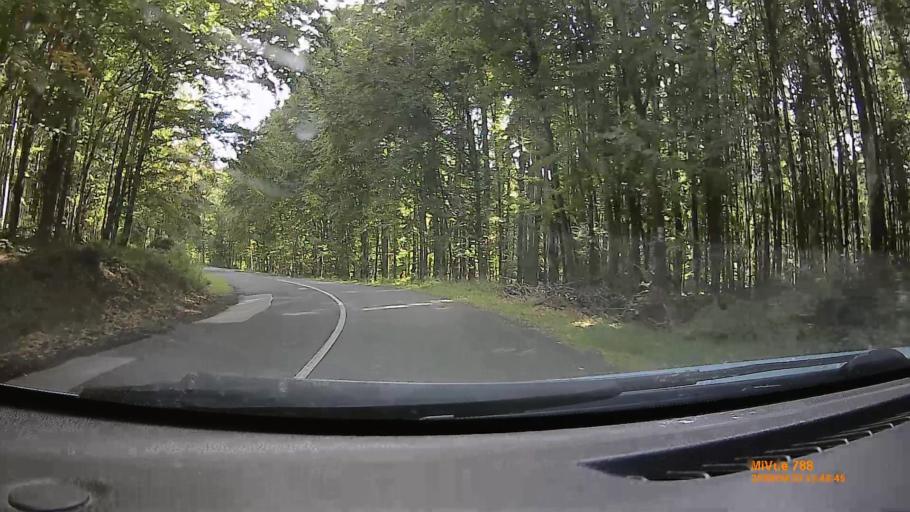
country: HU
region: Borsod-Abauj-Zemplen
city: Saly
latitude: 48.0639
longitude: 20.5850
